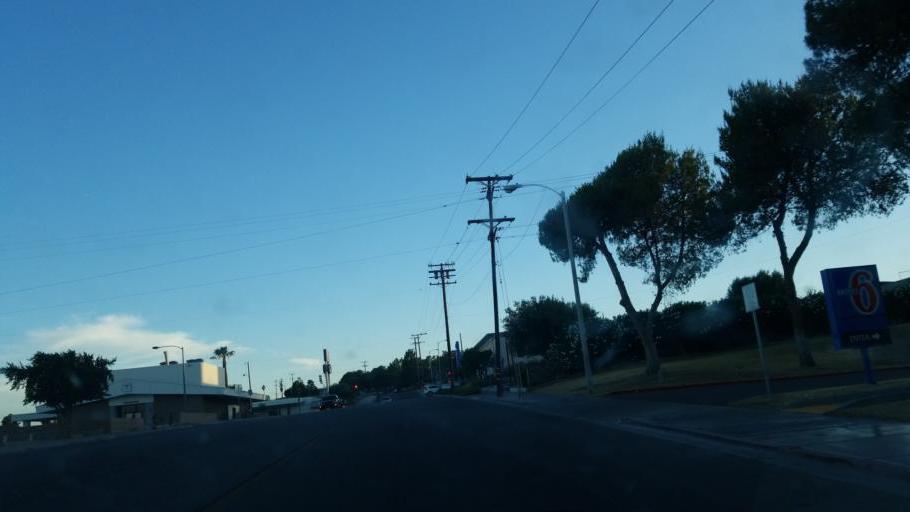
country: US
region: California
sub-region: San Bernardino County
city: Barstow
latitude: 34.8971
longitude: -117.0064
